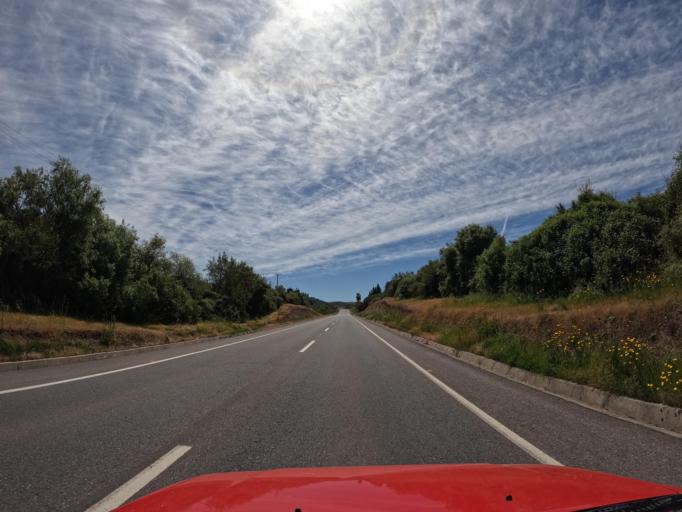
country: CL
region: Maule
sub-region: Provincia de Talca
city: Talca
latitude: -35.2615
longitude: -71.5422
